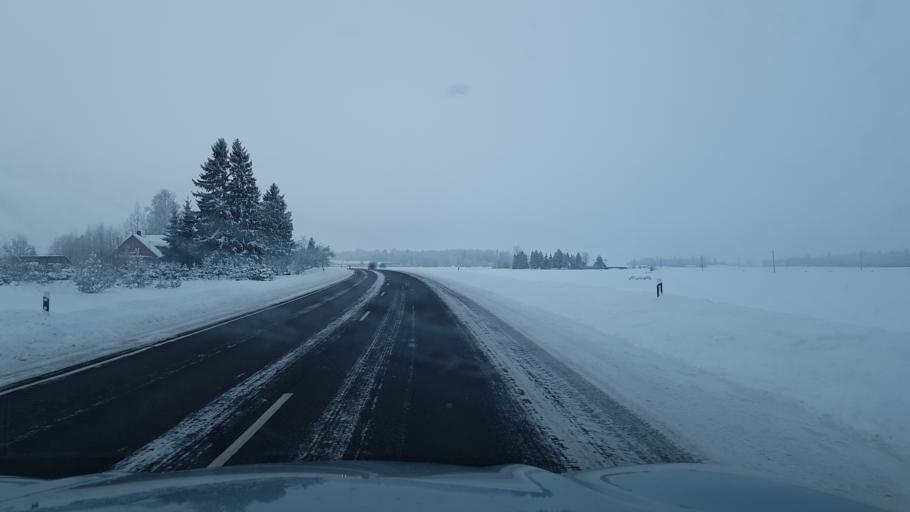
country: EE
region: Ida-Virumaa
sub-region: Johvi vald
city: Johvi
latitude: 59.2698
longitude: 27.3848
